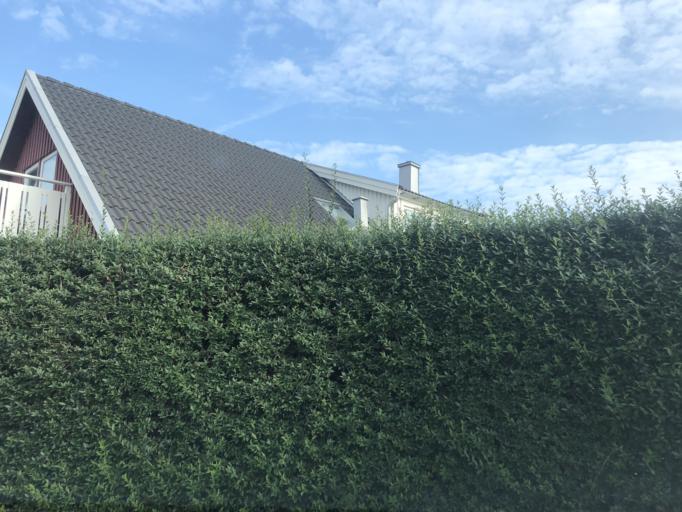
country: SE
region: Vaestra Goetaland
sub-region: Goteborg
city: Majorna
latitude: 57.6467
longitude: 11.8656
